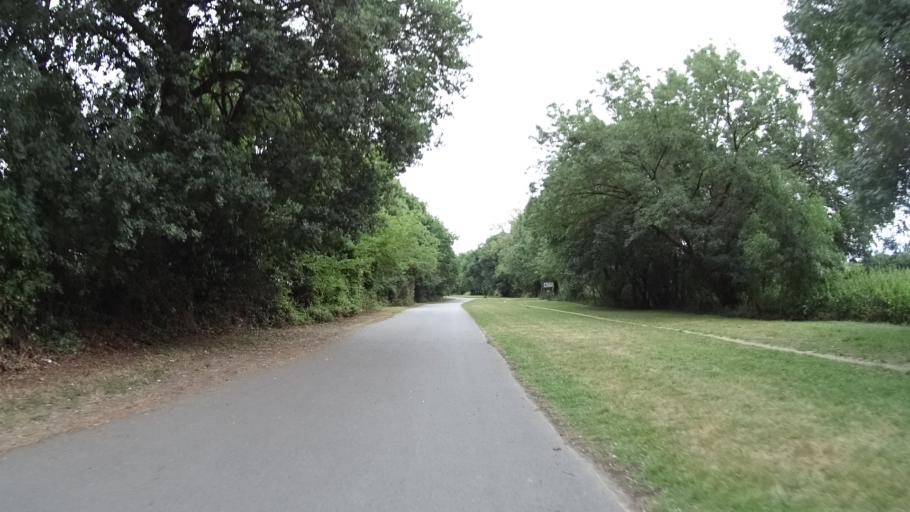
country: FR
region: Pays de la Loire
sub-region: Departement de la Loire-Atlantique
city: Thouare-sur-Loire
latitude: 47.2492
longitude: -1.4515
